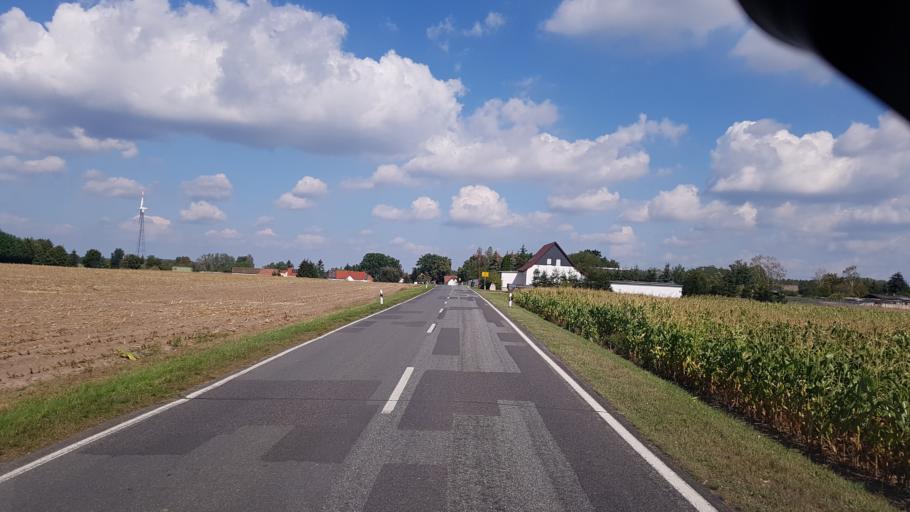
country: DE
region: Brandenburg
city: Drebkau
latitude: 51.6624
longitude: 14.2833
